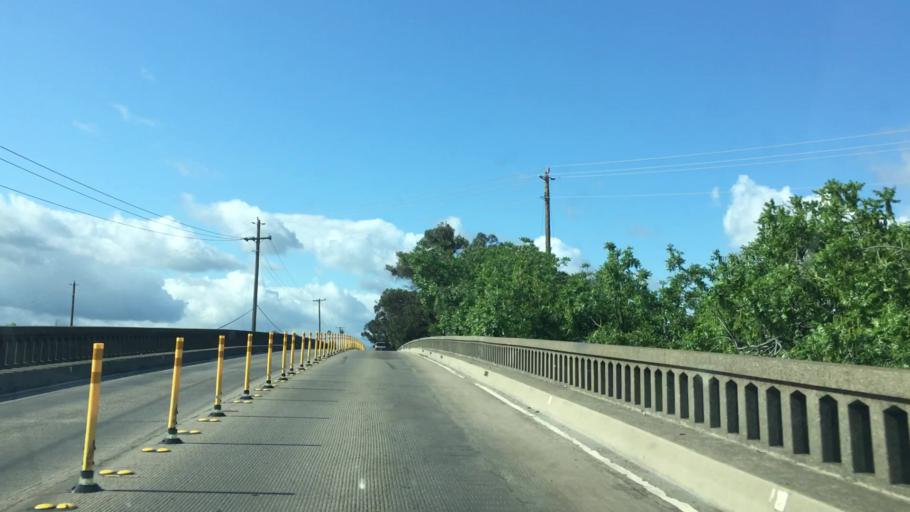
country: US
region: California
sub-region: Contra Costa County
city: Concord
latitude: 38.0039
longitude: -121.9996
